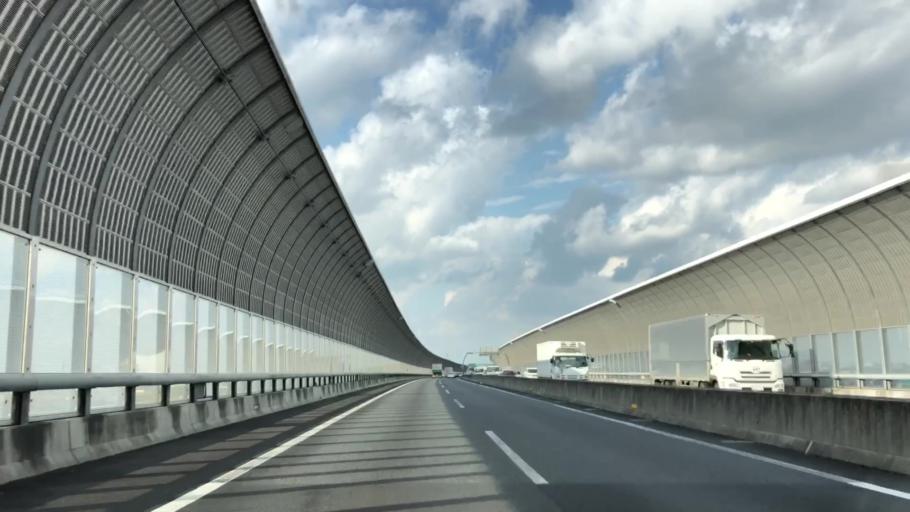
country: JP
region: Chiba
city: Matsudo
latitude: 35.8062
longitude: 139.8766
